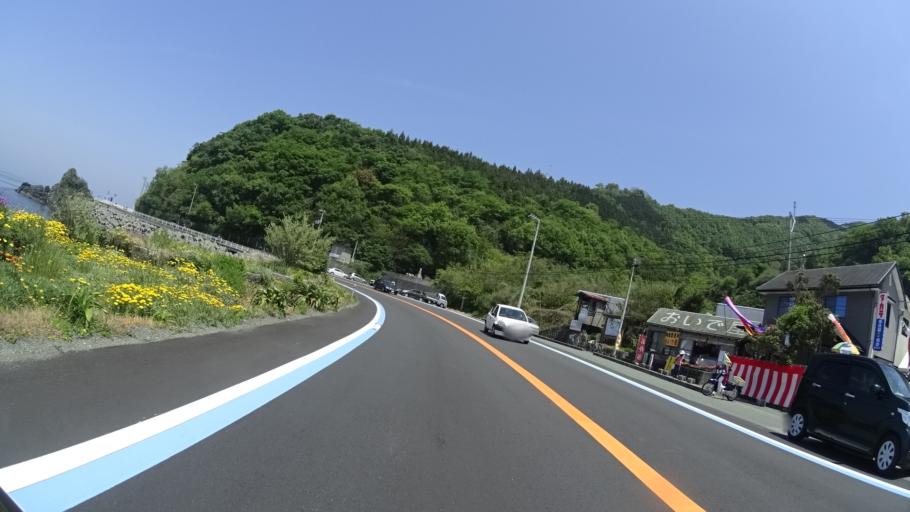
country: JP
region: Ehime
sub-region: Nishiuwa-gun
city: Ikata-cho
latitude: 33.5621
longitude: 132.4348
